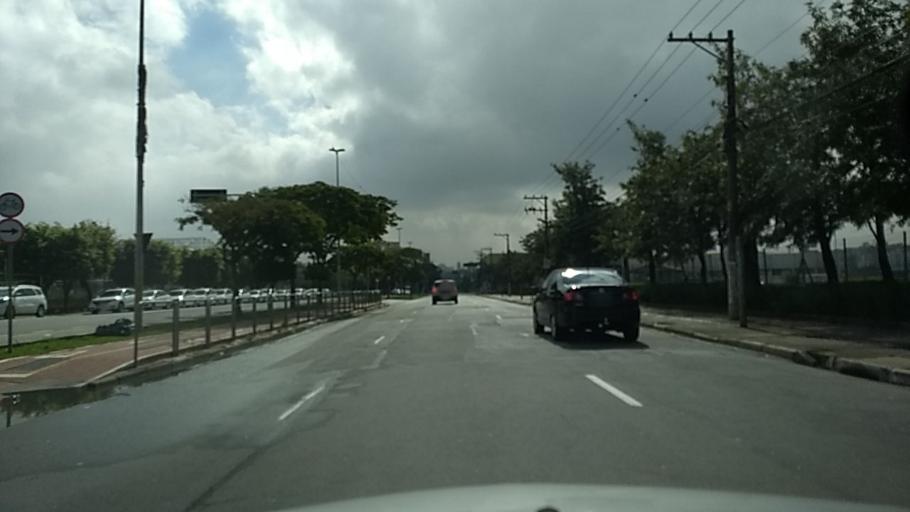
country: BR
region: Sao Paulo
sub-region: Sao Paulo
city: Sao Paulo
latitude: -23.5125
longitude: -46.6159
